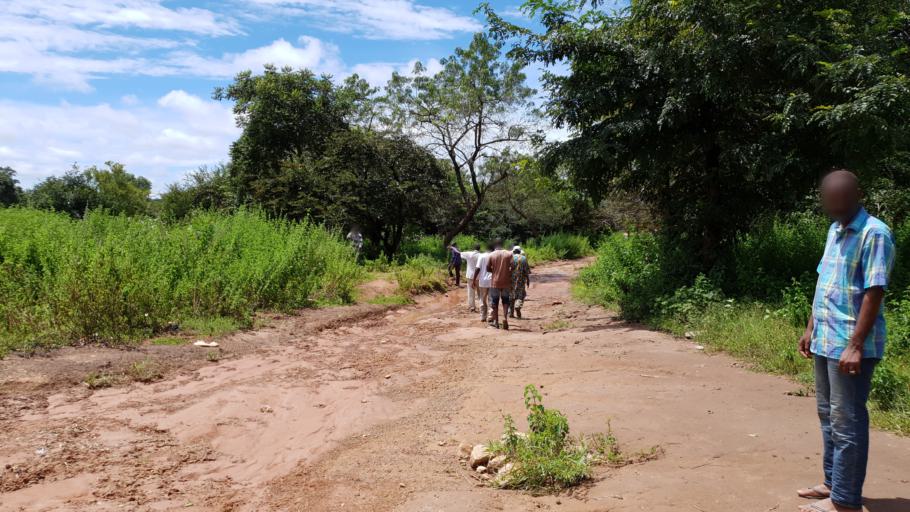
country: CI
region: Savanes
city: Tengrela
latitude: 10.3563
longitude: -6.9182
